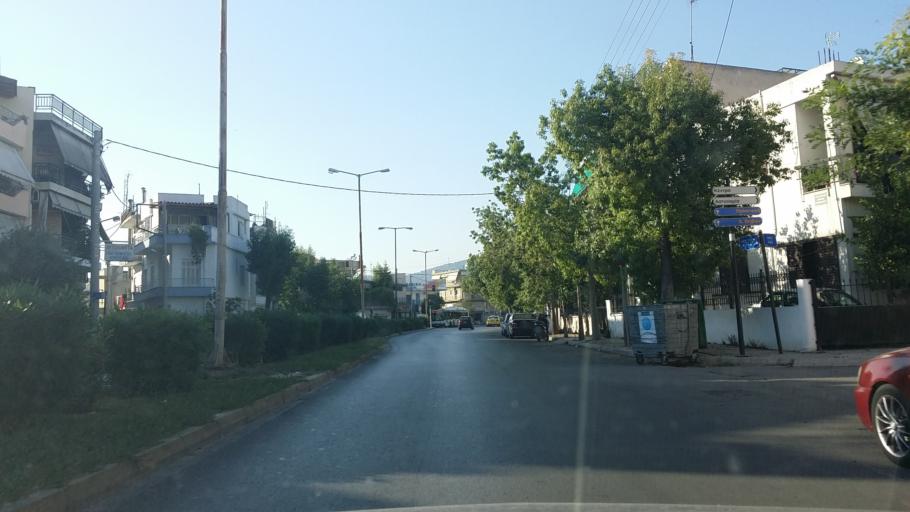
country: GR
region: Attica
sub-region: Nomarchia Athinas
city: Ilion
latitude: 38.0182
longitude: 23.7098
